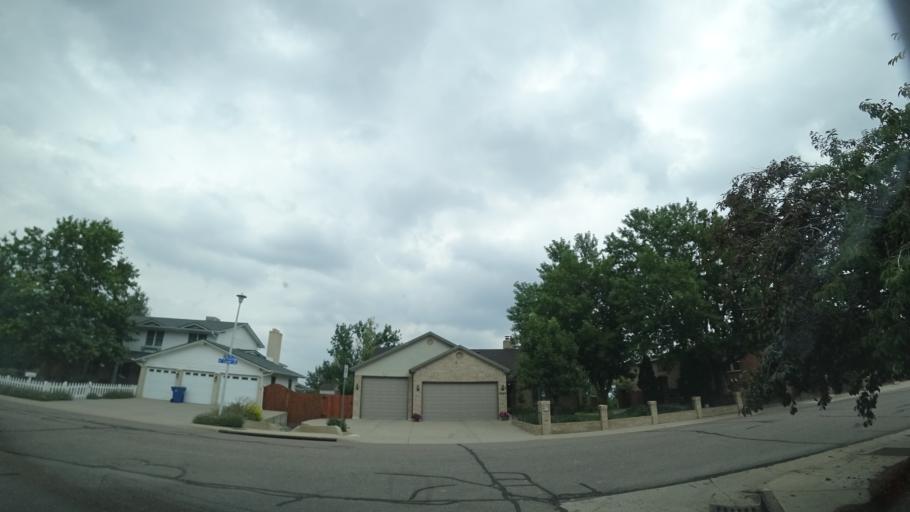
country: US
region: Colorado
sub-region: Jefferson County
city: West Pleasant View
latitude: 39.7068
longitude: -105.1593
